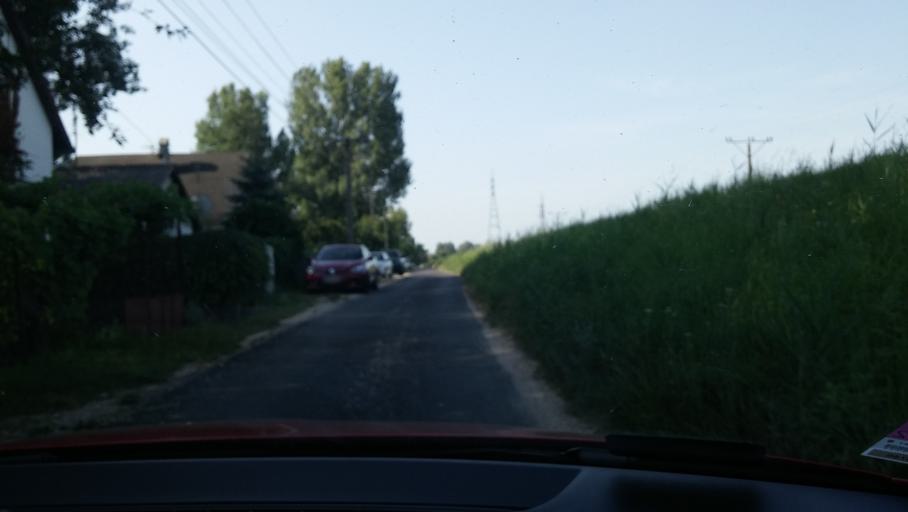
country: HU
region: Pest
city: Rackeve
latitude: 47.1834
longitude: 18.9478
